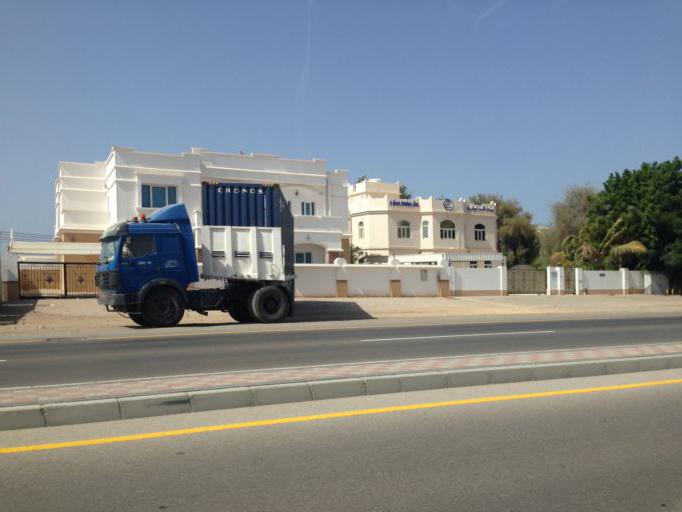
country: OM
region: Muhafazat Masqat
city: Bawshar
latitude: 23.6023
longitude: 58.3553
